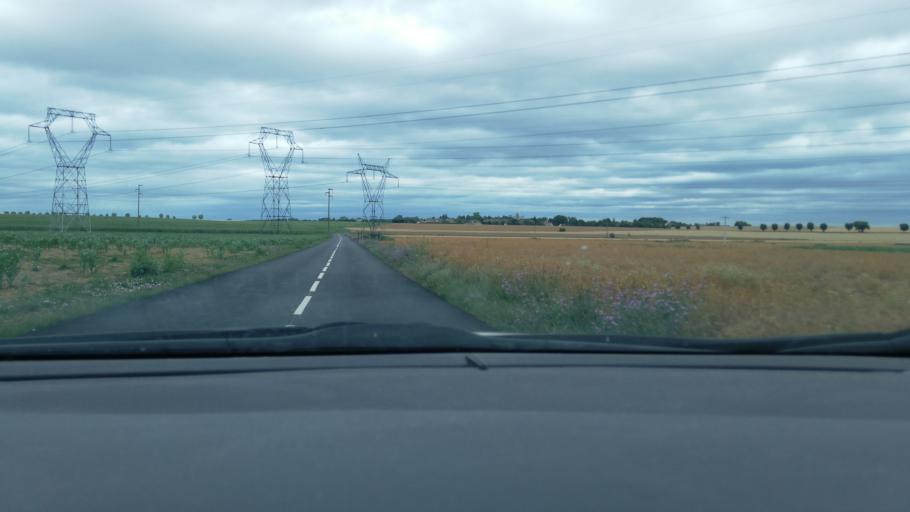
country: FR
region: Ile-de-France
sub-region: Departement du Val-d'Oise
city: Ennery
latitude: 49.0994
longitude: 2.1085
